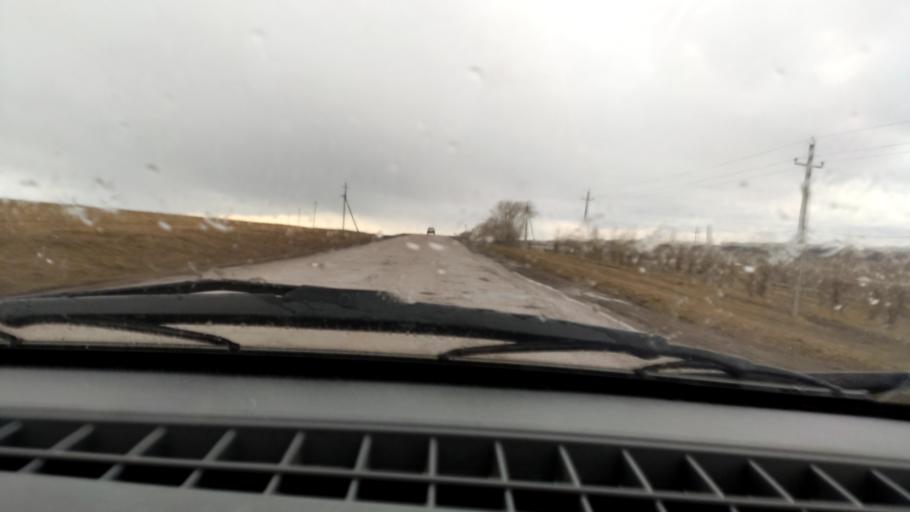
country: RU
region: Bashkortostan
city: Chekmagush
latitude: 55.1187
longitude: 54.7996
